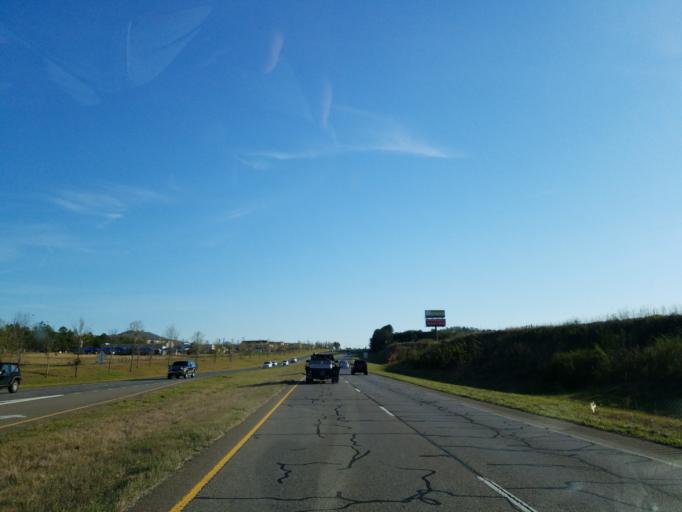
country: US
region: Georgia
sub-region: Gilmer County
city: Ellijay
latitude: 34.6644
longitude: -84.4887
